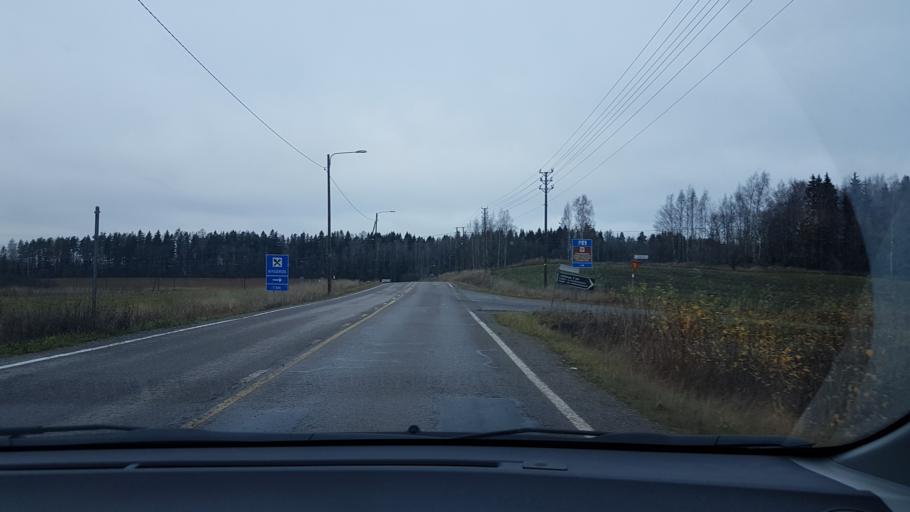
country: FI
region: Uusimaa
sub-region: Helsinki
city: Vantaa
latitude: 60.2761
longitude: 25.1367
